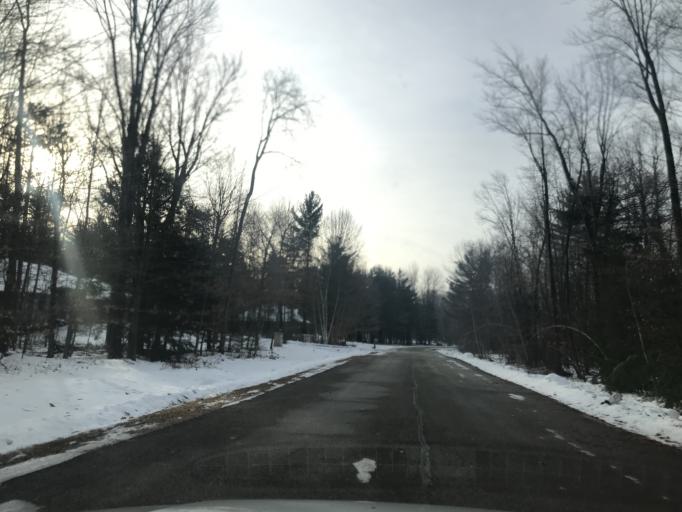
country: US
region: Wisconsin
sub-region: Brown County
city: Suamico
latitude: 44.6913
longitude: -88.0614
